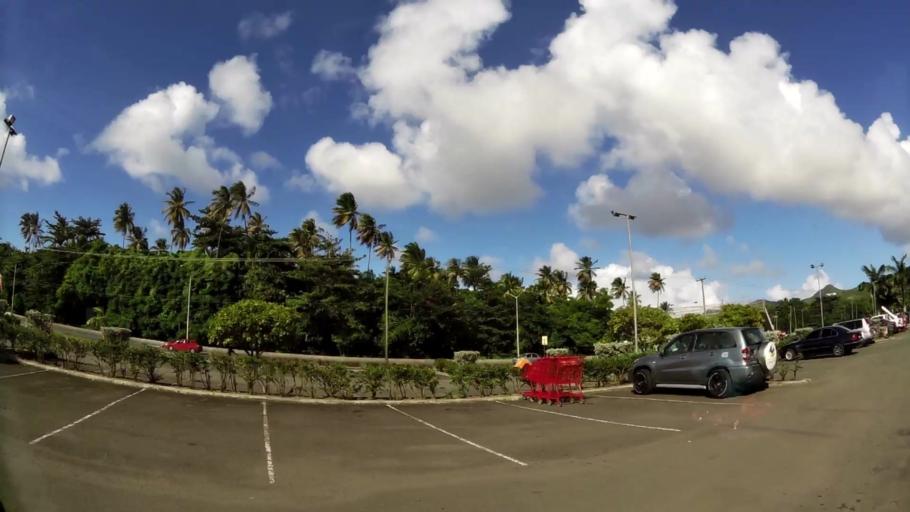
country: LC
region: Castries Quarter
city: Bisee
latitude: 14.0342
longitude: -60.9709
